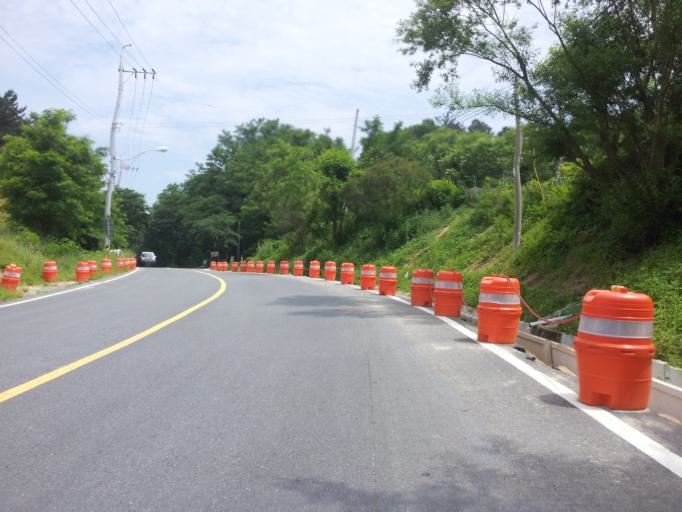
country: KR
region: Chungcheongbuk-do
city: Okcheon
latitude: 36.3821
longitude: 127.5187
